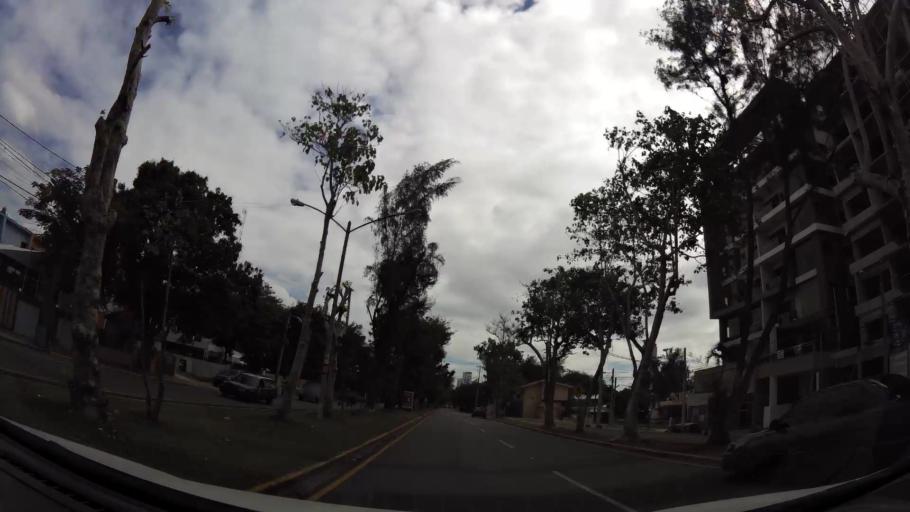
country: DO
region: Nacional
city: Bella Vista
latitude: 18.4479
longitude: -69.9542
